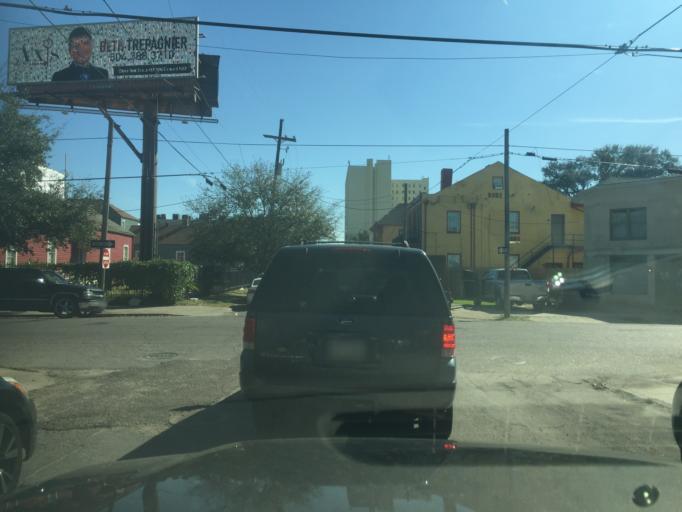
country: US
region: Louisiana
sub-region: Orleans Parish
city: New Orleans
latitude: 29.9428
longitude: -90.0764
